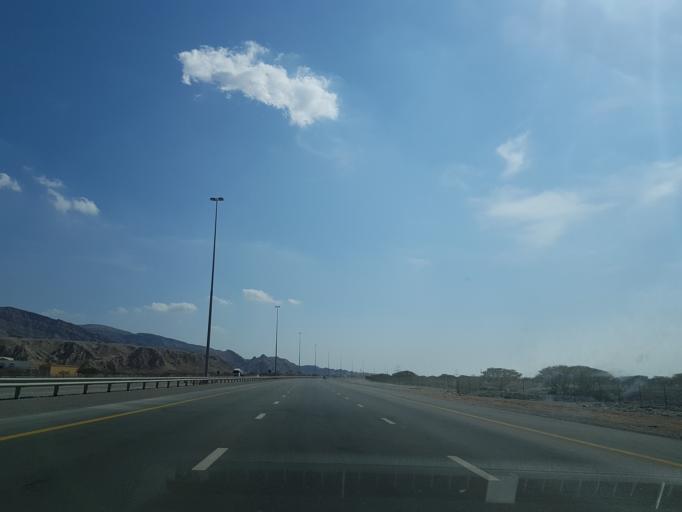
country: AE
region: Ra's al Khaymah
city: Ras al-Khaimah
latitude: 25.7886
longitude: 56.0312
